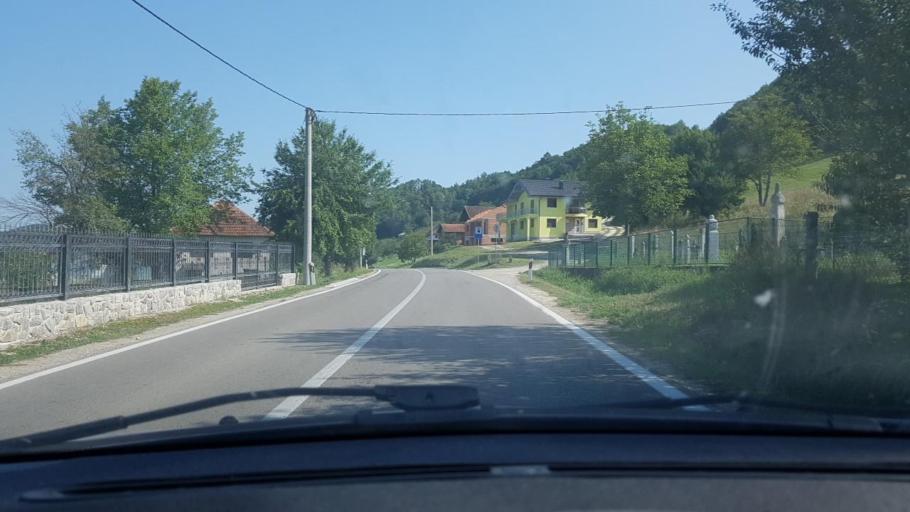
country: BA
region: Federation of Bosnia and Herzegovina
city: Pecigrad
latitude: 45.0840
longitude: 15.8889
